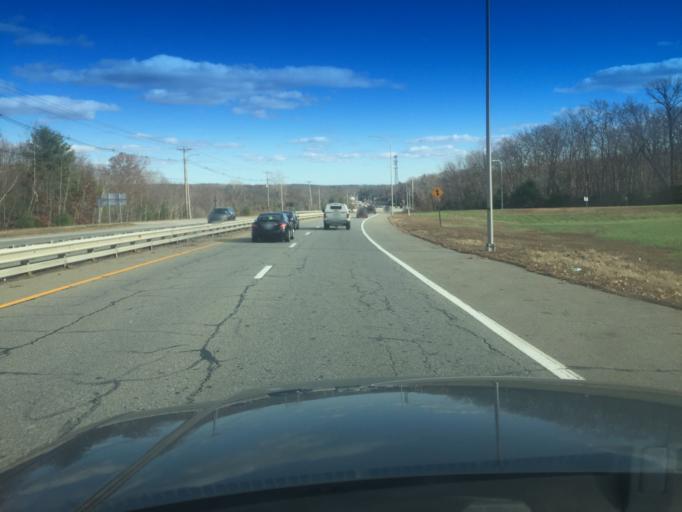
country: US
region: Rhode Island
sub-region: Providence County
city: Greenville
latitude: 41.8698
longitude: -71.5182
